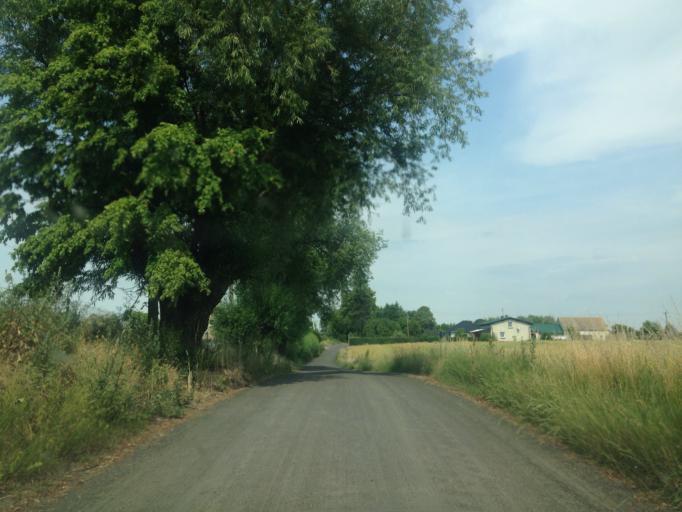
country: PL
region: Kujawsko-Pomorskie
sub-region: Powiat brodnicki
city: Bobrowo
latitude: 53.2730
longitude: 19.3114
